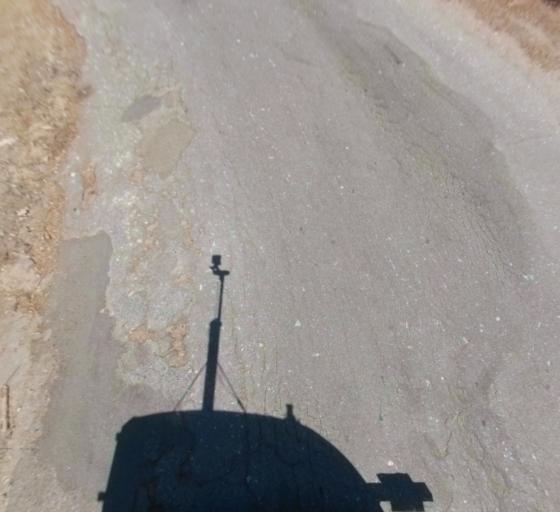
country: US
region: California
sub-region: Fresno County
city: Auberry
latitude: 37.1446
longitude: -119.4643
